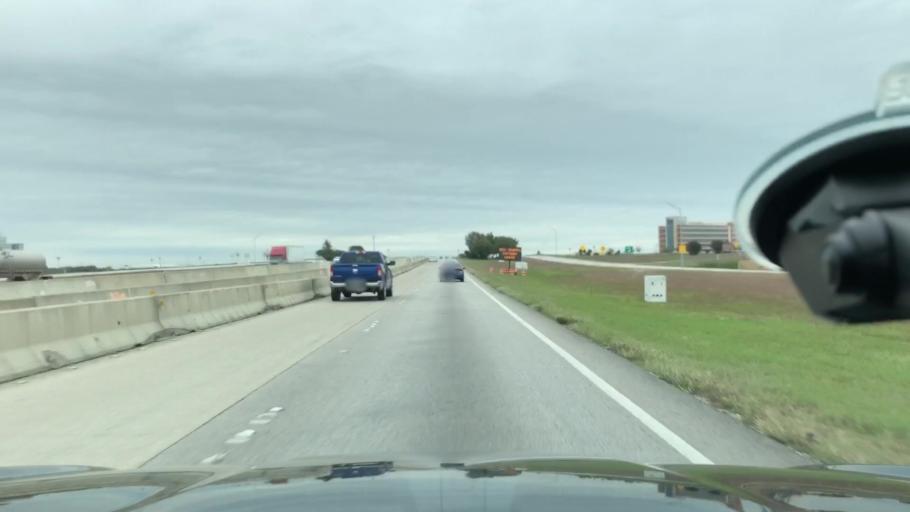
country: US
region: Texas
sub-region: Ellis County
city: Waxahachie
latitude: 32.4231
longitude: -96.8652
